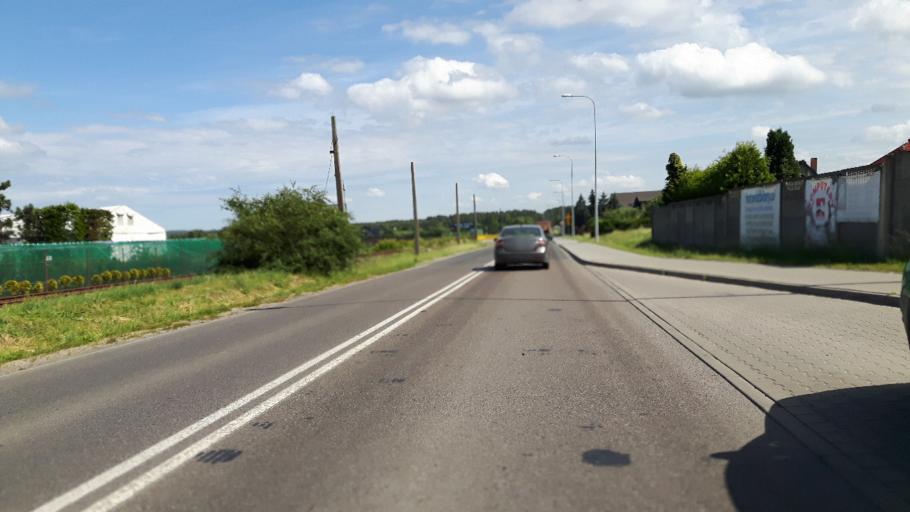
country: PL
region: Pomeranian Voivodeship
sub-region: Powiat wejherowski
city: Orle
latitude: 54.6351
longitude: 18.1392
